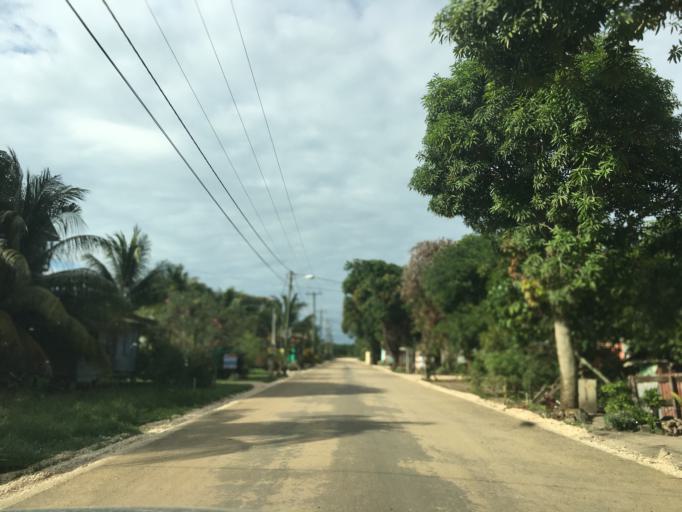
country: BZ
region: Stann Creek
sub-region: Dangriga
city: Dangriga
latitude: 16.8698
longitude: -88.2871
